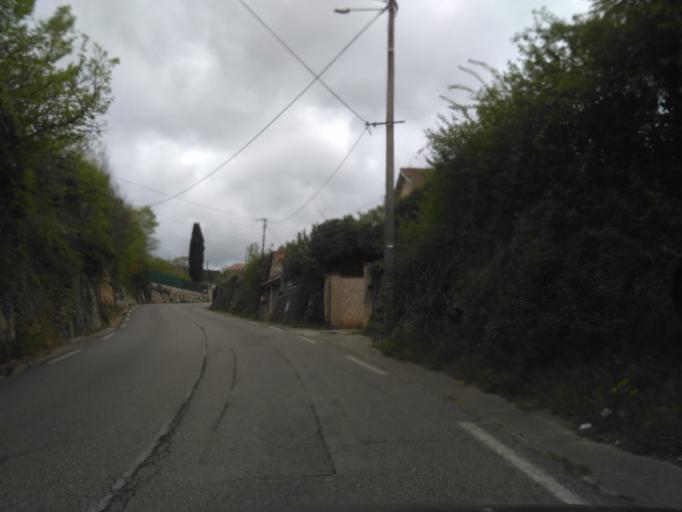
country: FR
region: Provence-Alpes-Cote d'Azur
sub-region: Departement du Var
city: Barjols
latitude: 43.5596
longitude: 6.0053
